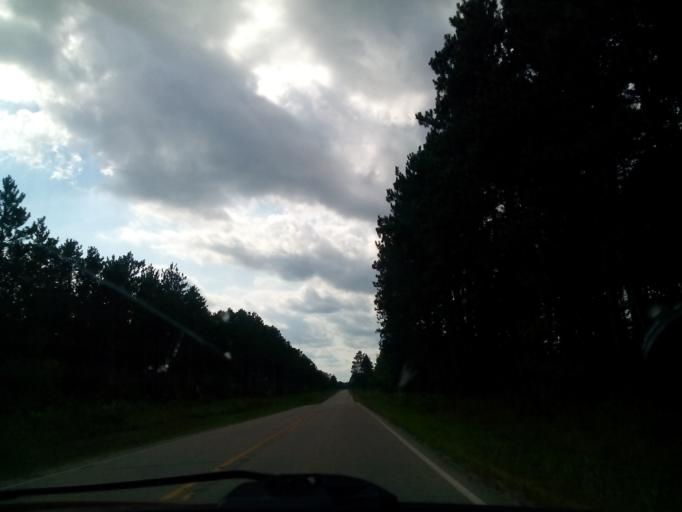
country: US
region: Michigan
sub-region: Dickinson County
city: Kingsford
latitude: 45.4021
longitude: -88.2261
